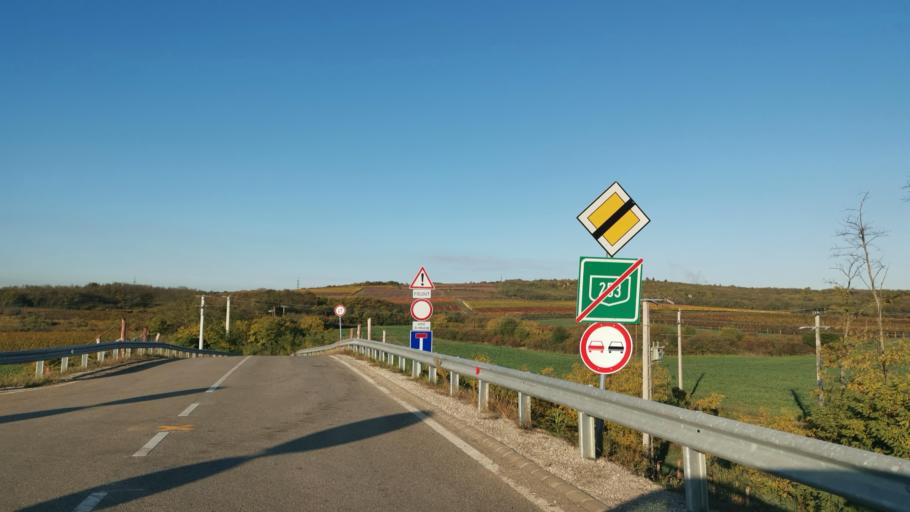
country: HU
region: Heves
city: Andornaktalya
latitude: 47.8391
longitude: 20.3967
